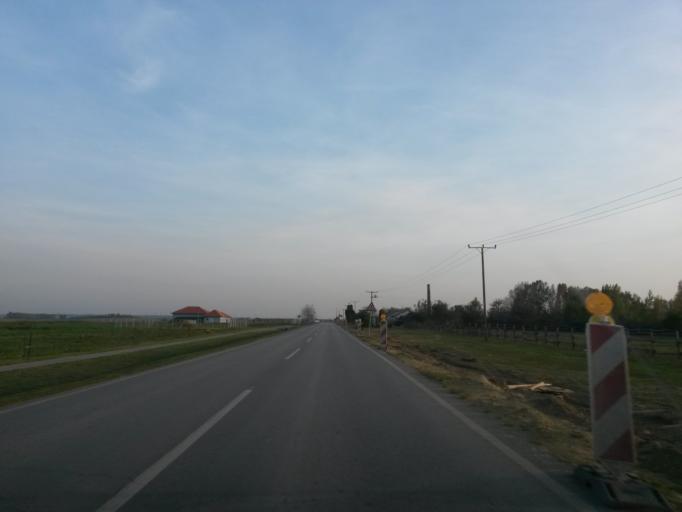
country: HR
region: Osjecko-Baranjska
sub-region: Grad Osijek
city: Karanac
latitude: 45.7368
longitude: 18.7277
